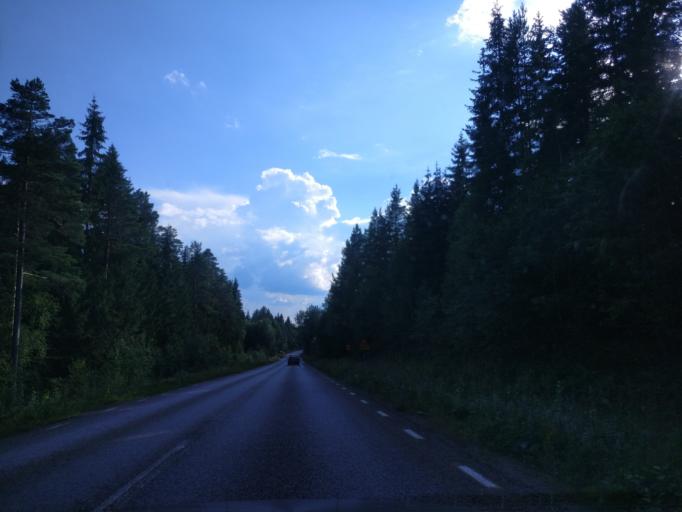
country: SE
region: Dalarna
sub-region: Ludvika Kommun
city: Ludvika
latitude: 60.2803
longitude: 15.0868
